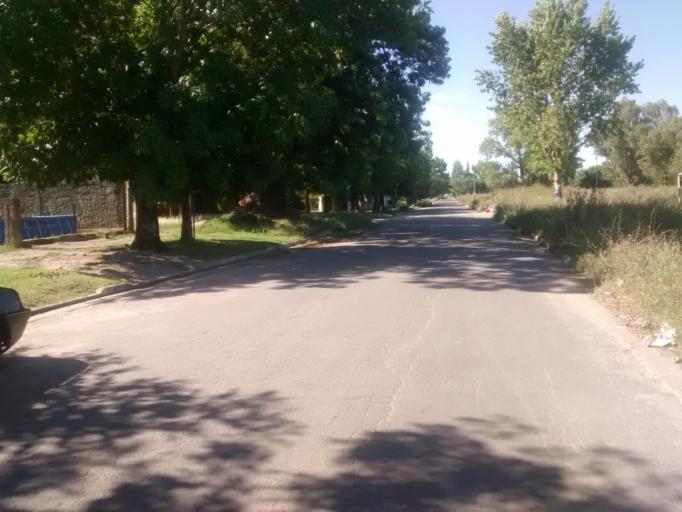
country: AR
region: Buenos Aires
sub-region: Partido de La Plata
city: La Plata
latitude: -34.9332
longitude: -57.9008
